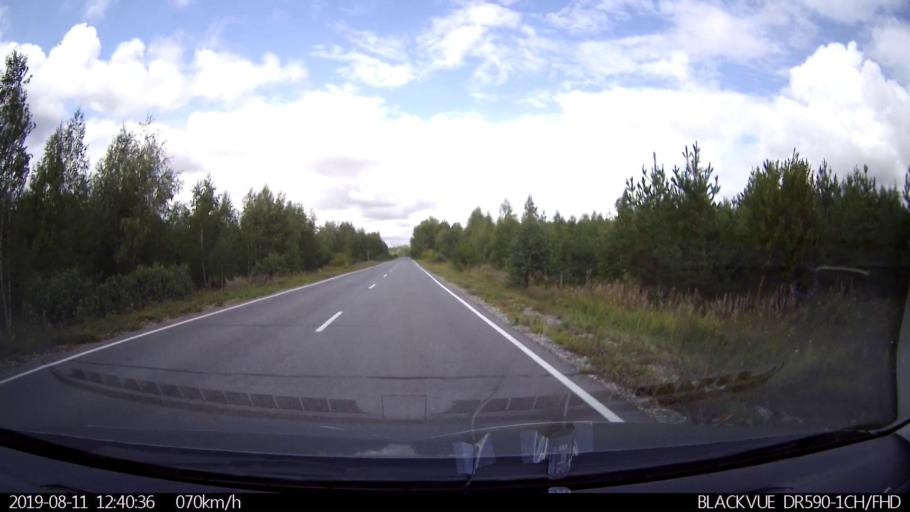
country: RU
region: Ulyanovsk
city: Ignatovka
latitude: 53.8396
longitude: 47.7783
